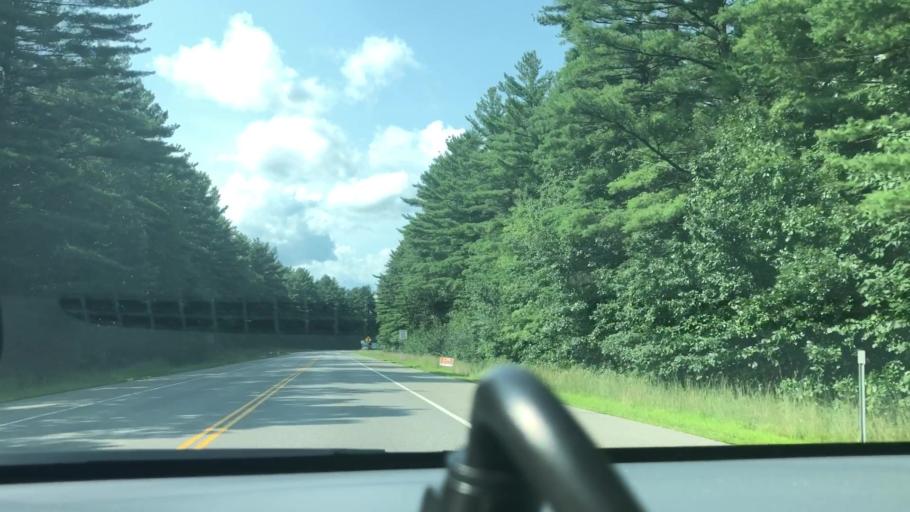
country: US
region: New Hampshire
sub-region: Hillsborough County
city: Pinardville
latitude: 43.0029
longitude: -71.5253
